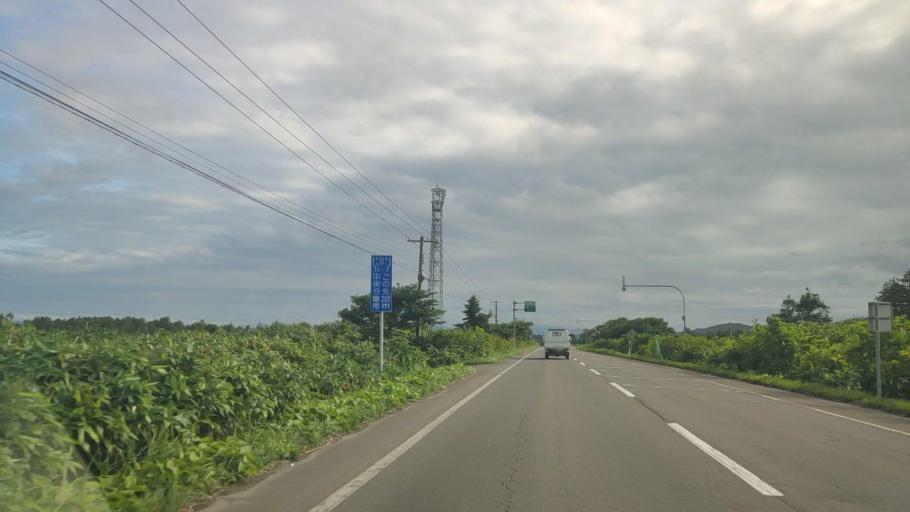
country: JP
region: Hokkaido
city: Niseko Town
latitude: 42.4578
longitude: 140.3344
